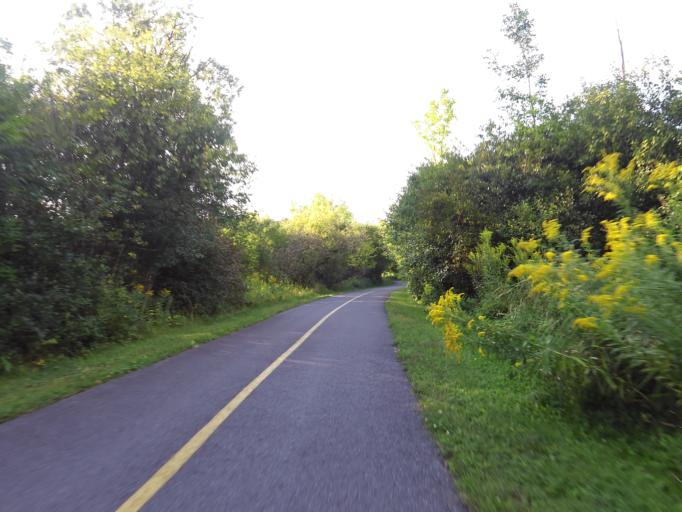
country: CA
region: Ontario
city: Bells Corners
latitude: 45.3420
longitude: -75.8745
